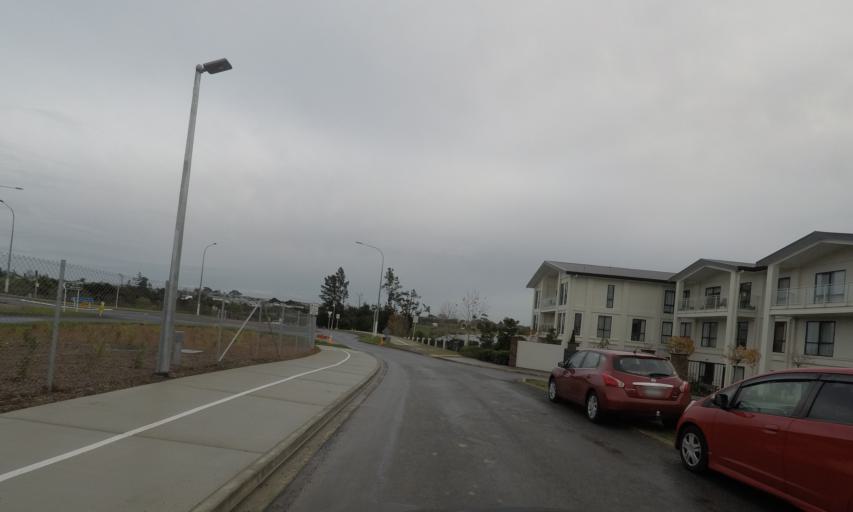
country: NZ
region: Auckland
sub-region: Auckland
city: Rosebank
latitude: -36.7902
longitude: 174.6547
